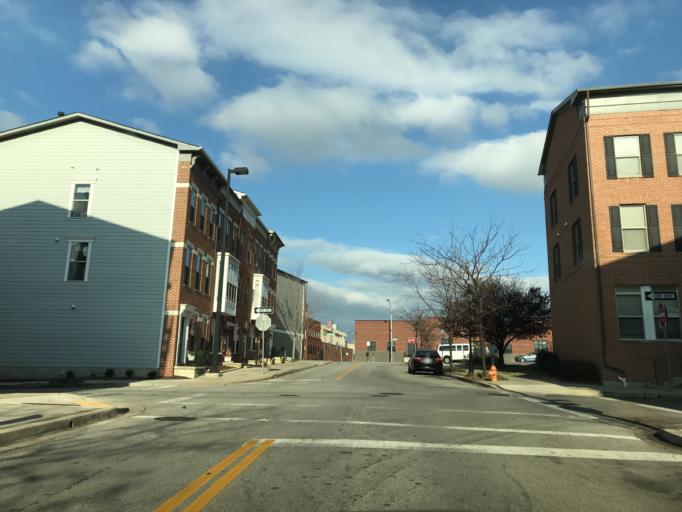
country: US
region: Maryland
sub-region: City of Baltimore
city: Baltimore
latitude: 39.2898
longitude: -76.6028
